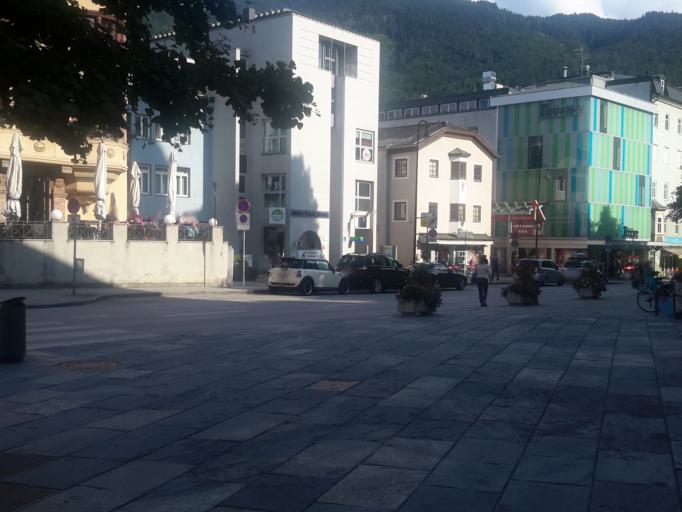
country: AT
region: Tyrol
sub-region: Politischer Bezirk Kufstein
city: Kufstein
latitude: 47.5830
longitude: 12.1706
